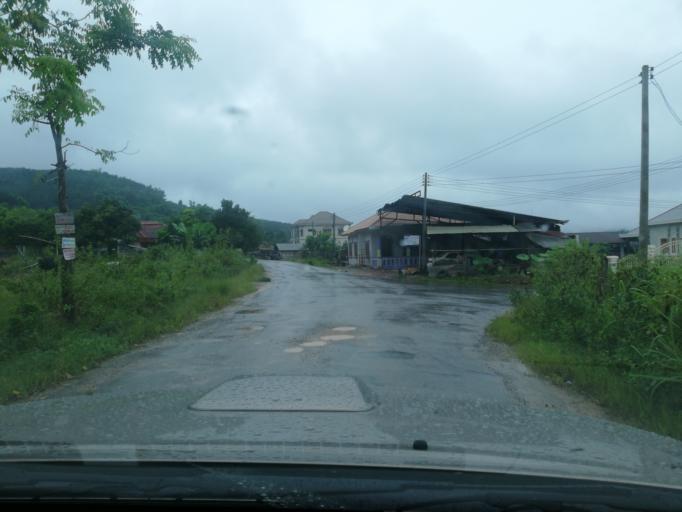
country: LA
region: Loungnamtha
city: Louang Namtha
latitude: 20.9993
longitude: 101.4005
